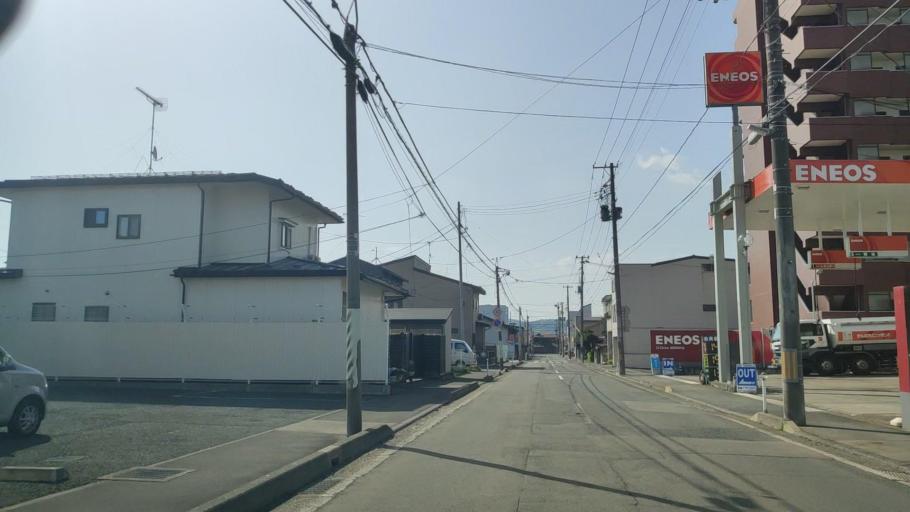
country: JP
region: Iwate
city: Morioka-shi
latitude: 39.6963
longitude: 141.1534
